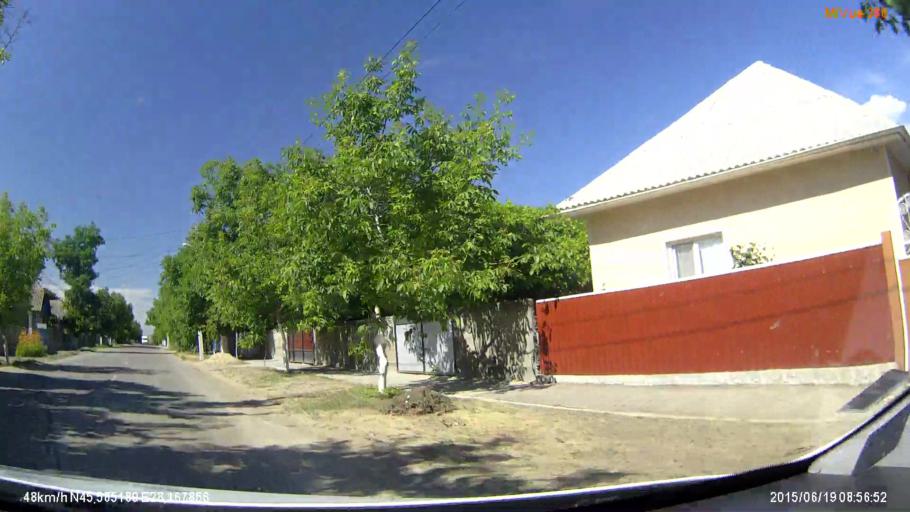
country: MD
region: Cahul
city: Giurgiulesti
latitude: 45.5851
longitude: 28.1679
